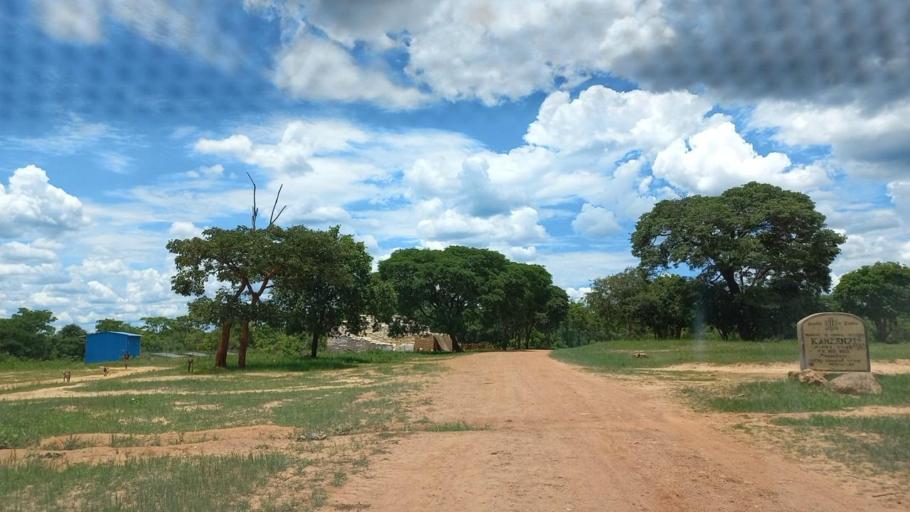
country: ZM
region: North-Western
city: Mwinilunga
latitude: -12.5464
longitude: 24.2005
